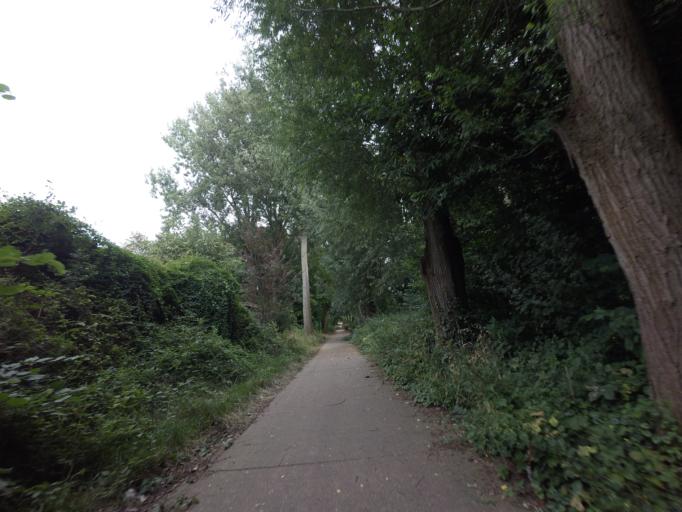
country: BE
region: Flanders
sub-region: Provincie Vlaams-Brabant
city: Grimbergen
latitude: 50.9142
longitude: 4.3610
